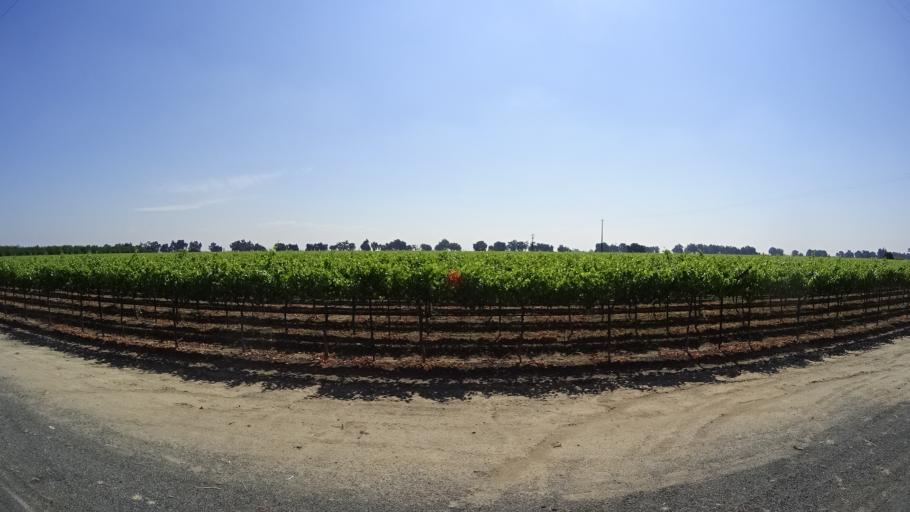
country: US
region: California
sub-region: Fresno County
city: Kingsburg
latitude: 36.4697
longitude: -119.5508
